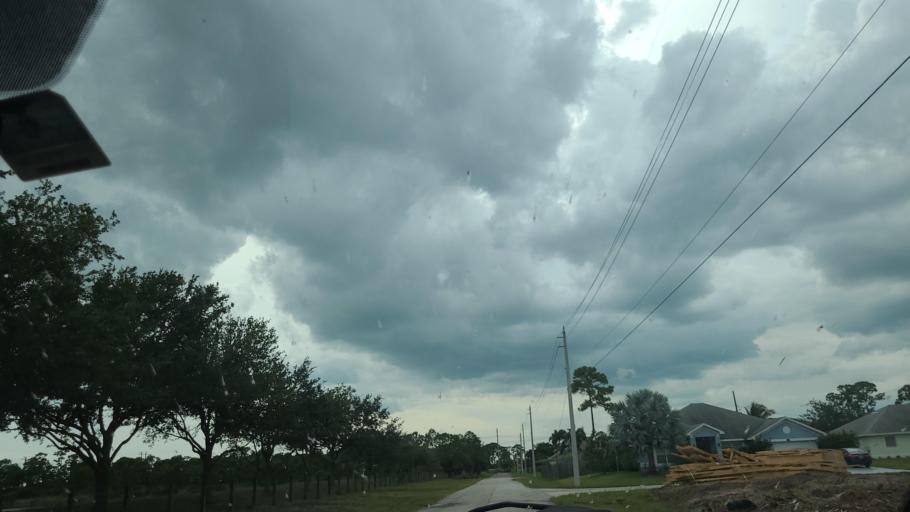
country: US
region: Florida
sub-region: Saint Lucie County
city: Port Saint Lucie
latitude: 27.2499
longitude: -80.4113
